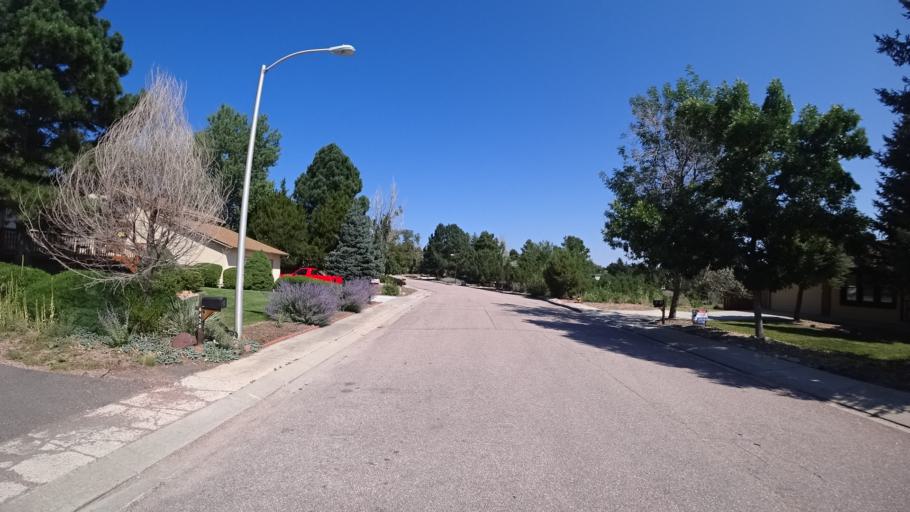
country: US
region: Colorado
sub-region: El Paso County
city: Air Force Academy
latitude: 38.9238
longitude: -104.8240
